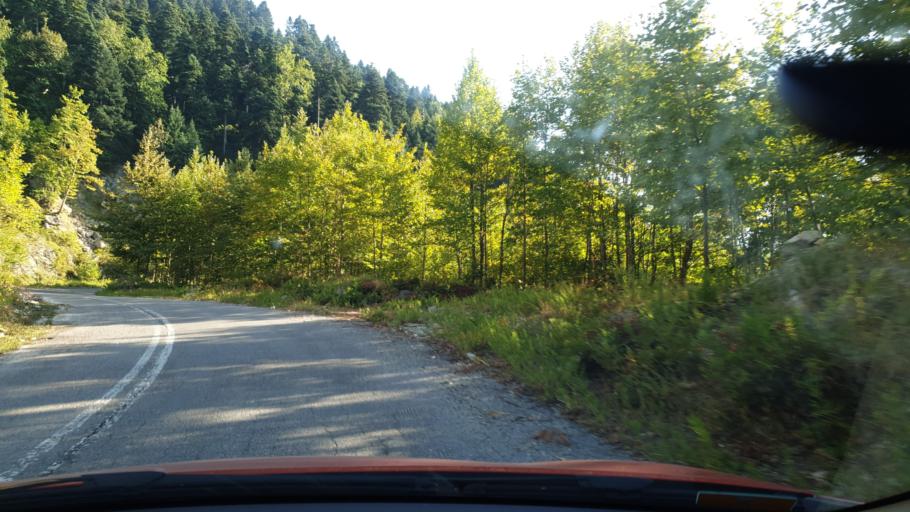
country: GR
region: Central Greece
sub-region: Nomos Evvoias
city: Yimnon
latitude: 38.6063
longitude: 23.9208
